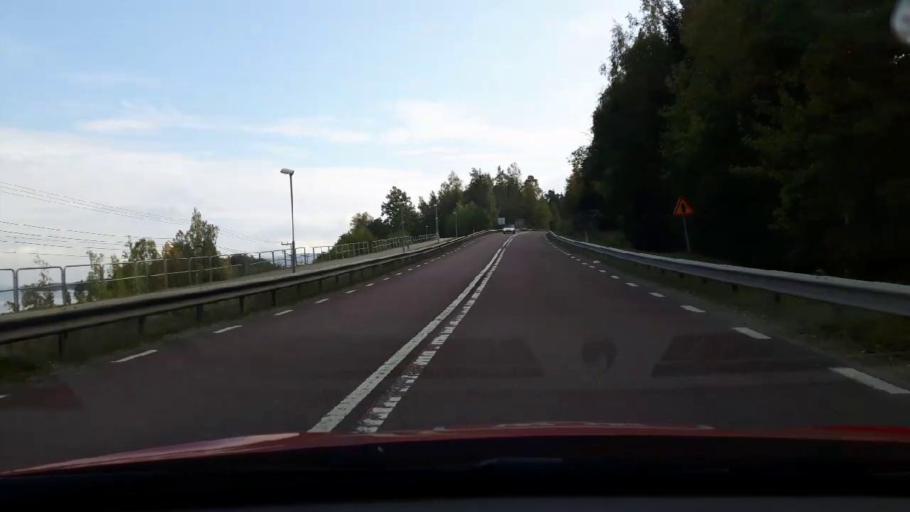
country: SE
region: Gaevleborg
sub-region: Bollnas Kommun
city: Kilafors
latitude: 61.2212
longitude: 16.5796
